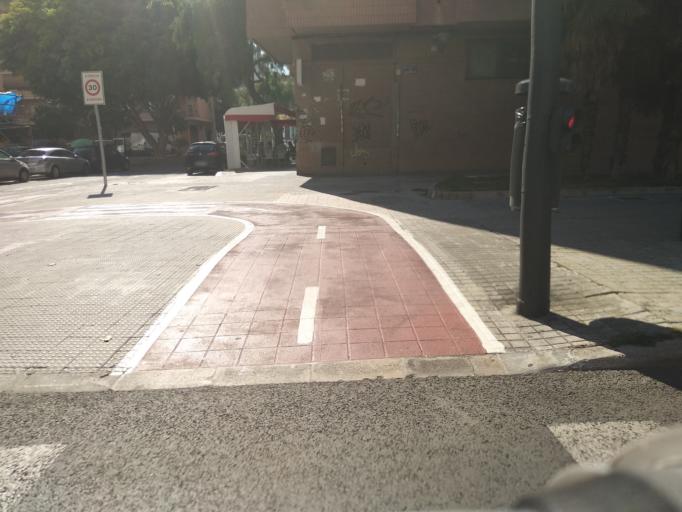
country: ES
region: Valencia
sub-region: Provincia de Valencia
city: Alboraya
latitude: 39.4777
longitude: -0.3516
